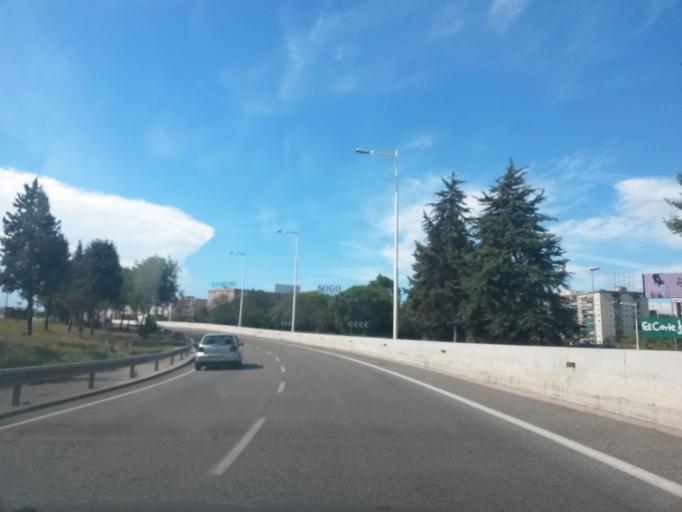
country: ES
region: Catalonia
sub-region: Provincia de Barcelona
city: Sant Adria de Besos
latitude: 41.4257
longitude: 2.2155
